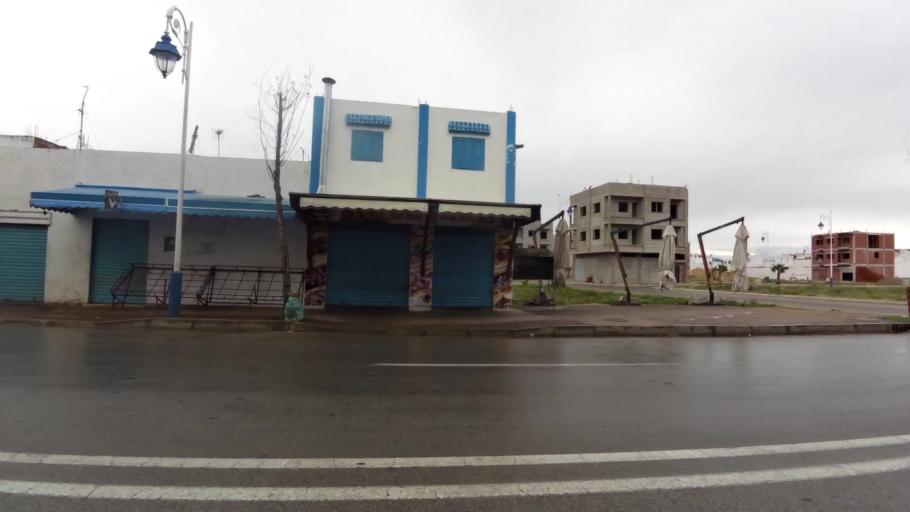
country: MA
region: Tanger-Tetouan
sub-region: Tetouan
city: Martil
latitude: 35.6256
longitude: -5.2917
